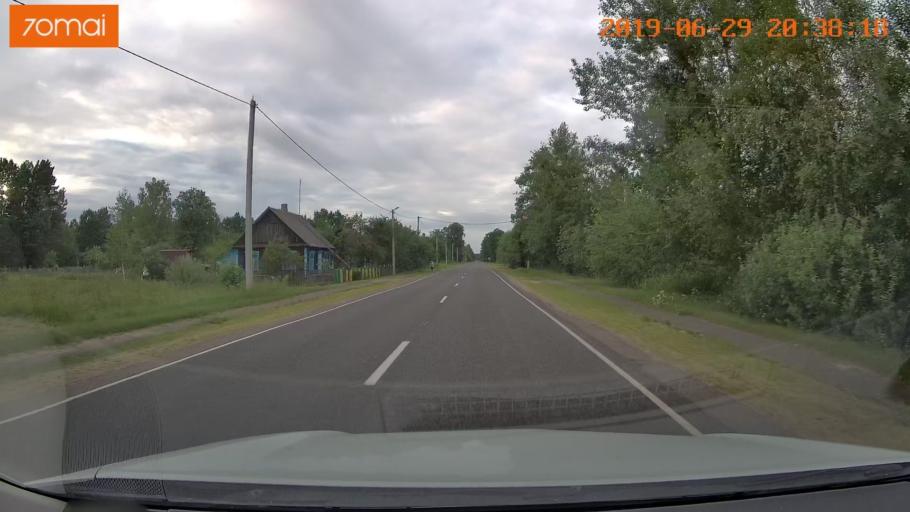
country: BY
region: Brest
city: Hantsavichy
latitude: 52.5485
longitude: 26.3648
